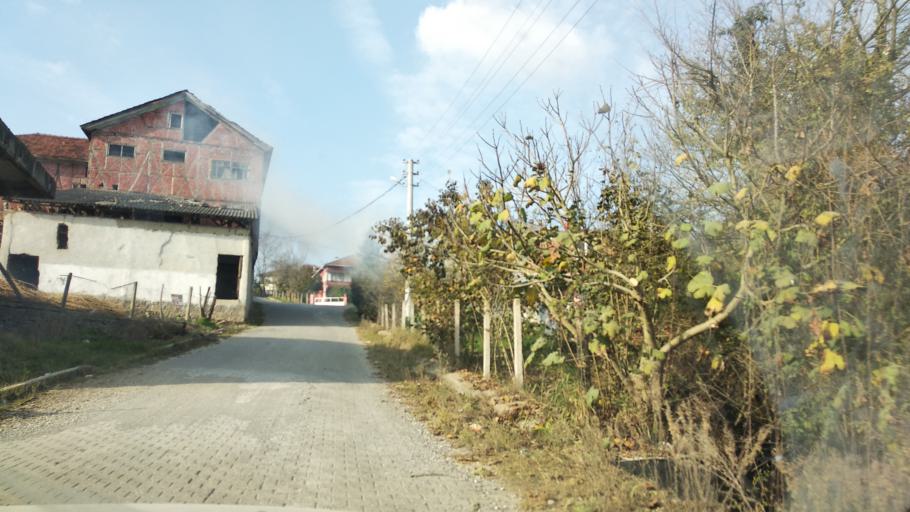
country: TR
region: Sakarya
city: Karasu
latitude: 41.0554
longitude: 30.6282
